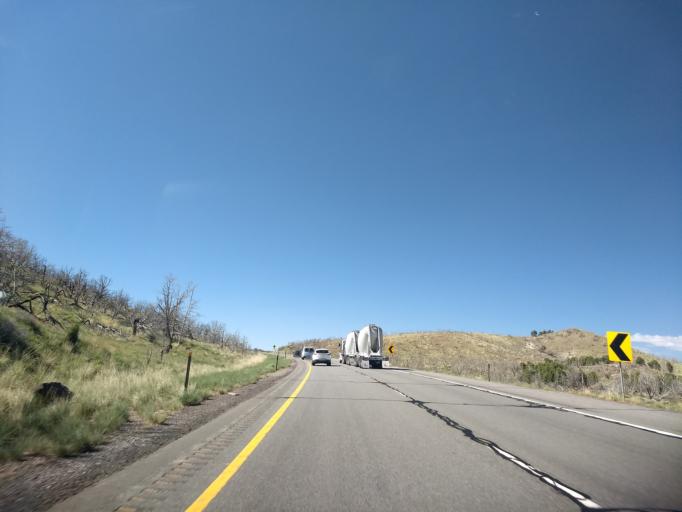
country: US
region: Utah
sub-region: Beaver County
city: Beaver
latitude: 38.6301
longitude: -112.6081
